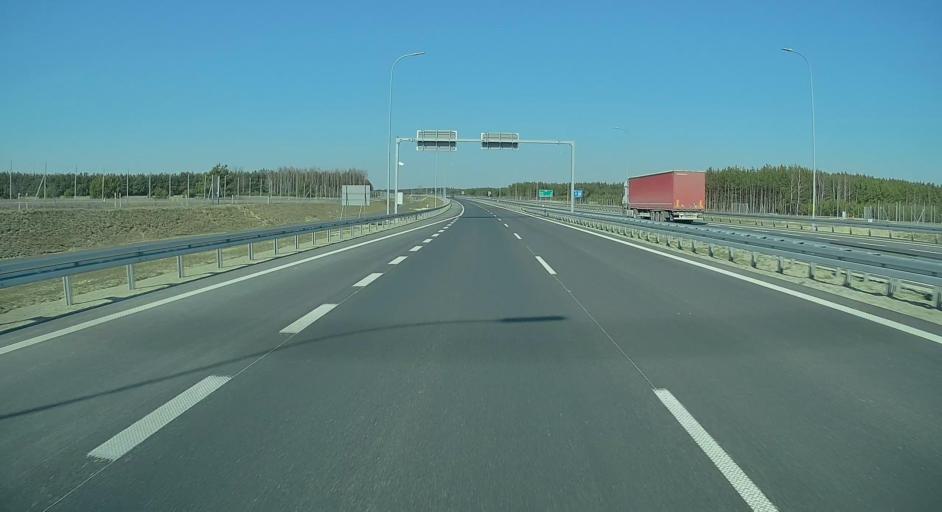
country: PL
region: Subcarpathian Voivodeship
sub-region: Powiat nizanski
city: Jezowe
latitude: 50.3736
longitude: 22.1818
